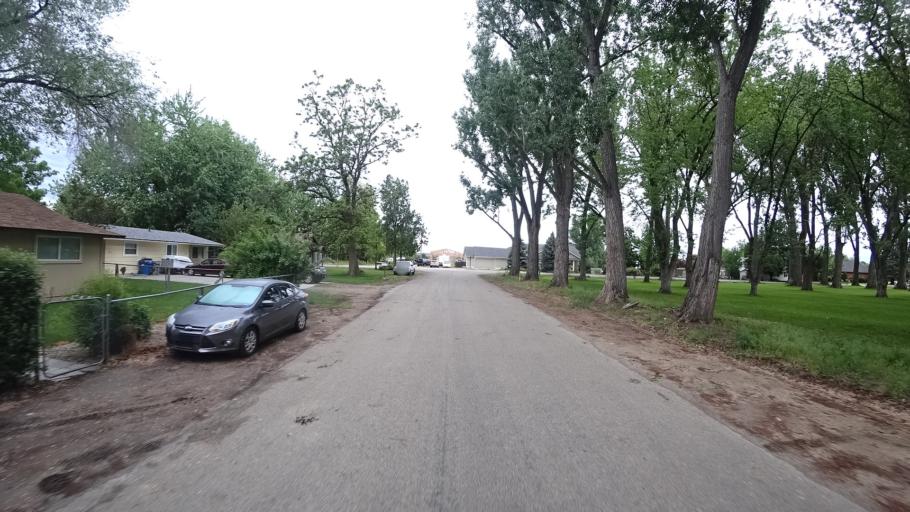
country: US
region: Idaho
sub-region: Ada County
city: Star
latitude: 43.6951
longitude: -116.4955
